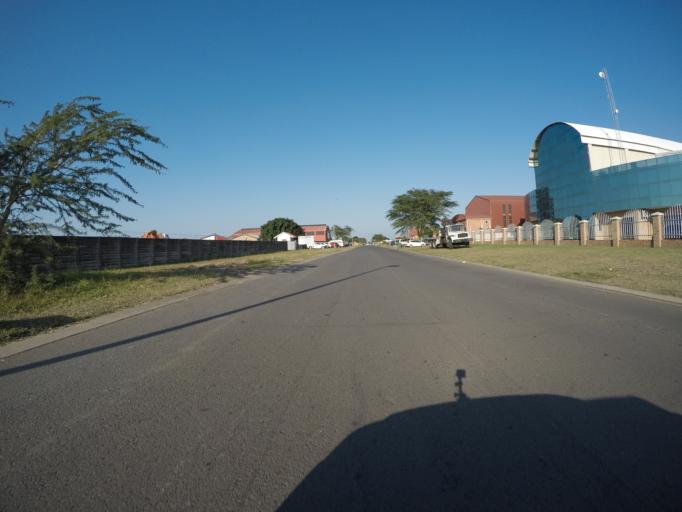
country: ZA
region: KwaZulu-Natal
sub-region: uThungulu District Municipality
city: Richards Bay
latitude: -28.7374
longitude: 32.0395
